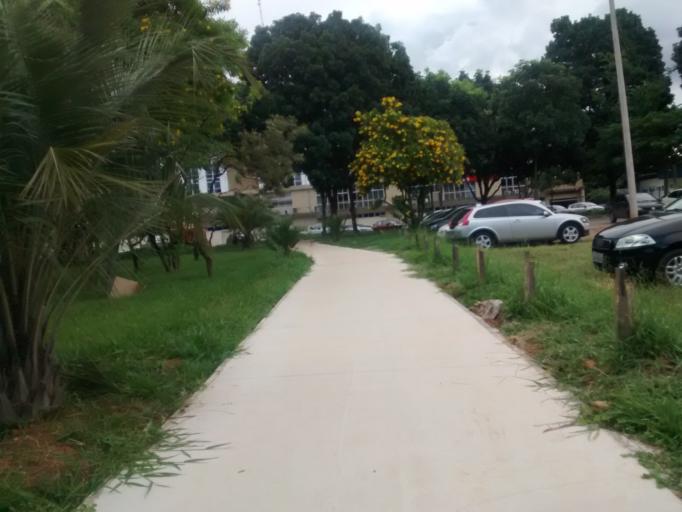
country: BR
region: Federal District
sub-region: Brasilia
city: Brasilia
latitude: -15.7477
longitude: -47.8947
